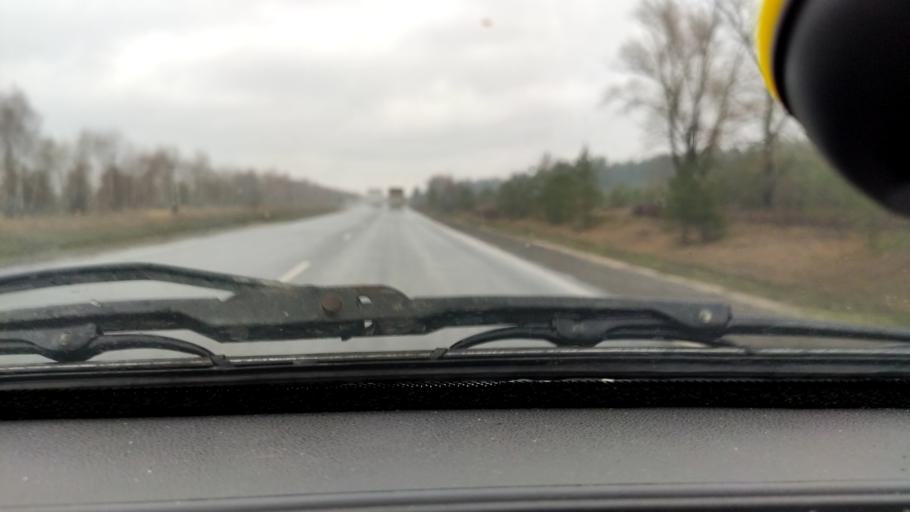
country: RU
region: Samara
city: Povolzhskiy
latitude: 53.5948
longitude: 49.5854
